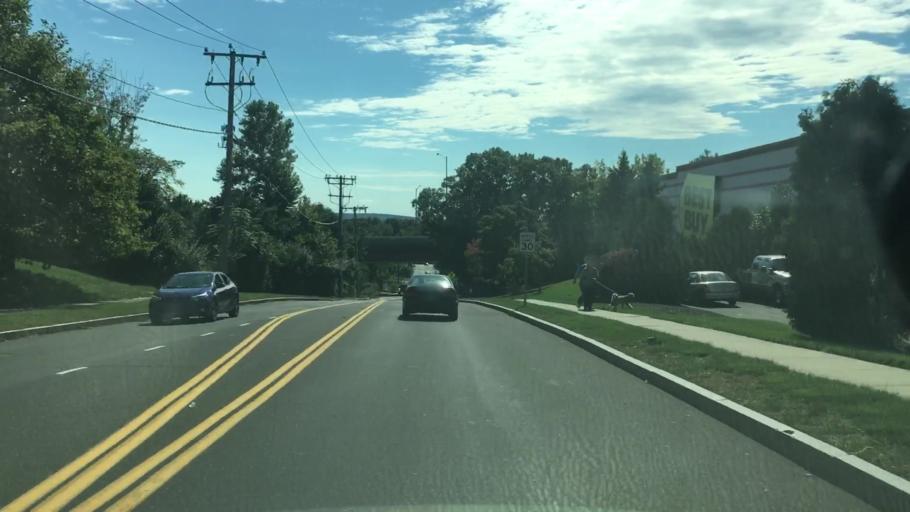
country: US
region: Connecticut
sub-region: Hartford County
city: Manchester
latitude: 41.8077
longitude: -72.5348
